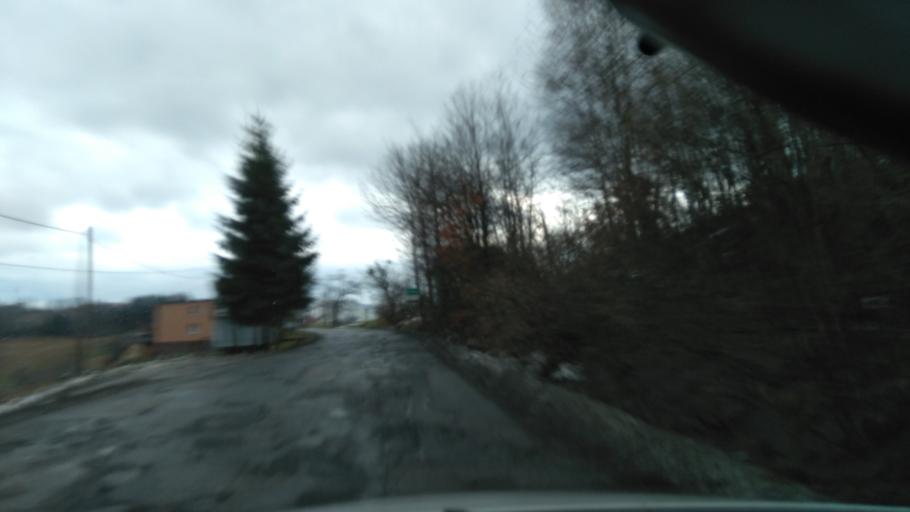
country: PL
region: Silesian Voivodeship
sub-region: Powiat cieszynski
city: Istebna
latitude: 49.5500
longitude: 18.8949
